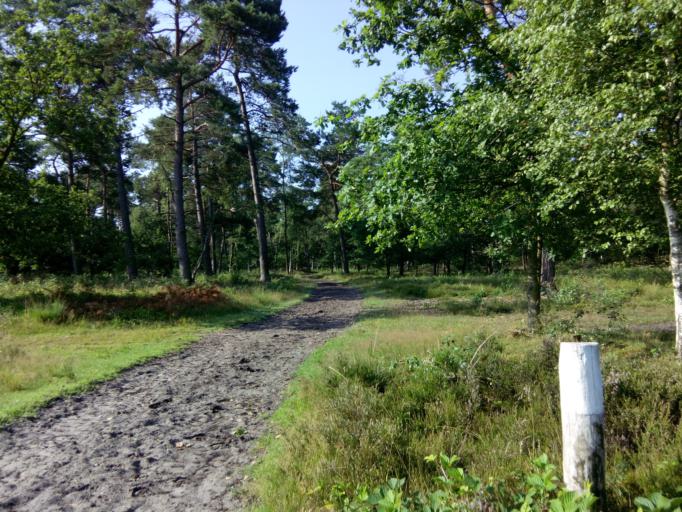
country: NL
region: Utrecht
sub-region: Gemeente Utrechtse Heuvelrug
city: Maarn
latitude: 52.0954
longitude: 5.3651
